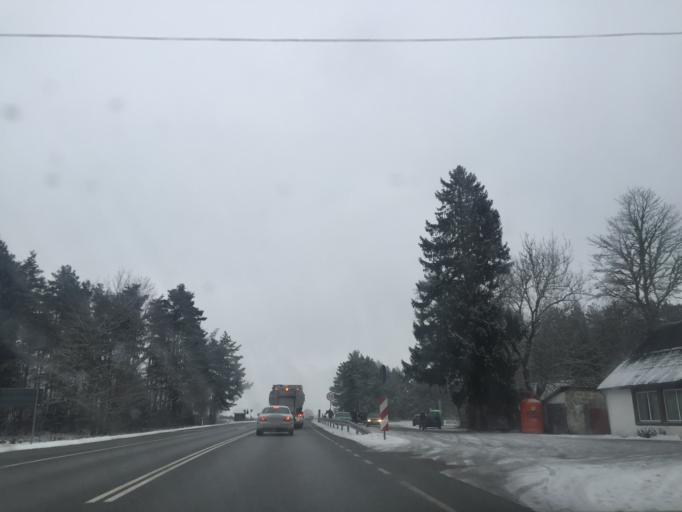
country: EE
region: Laeaene
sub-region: Lihula vald
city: Lihula
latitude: 58.6624
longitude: 23.7311
